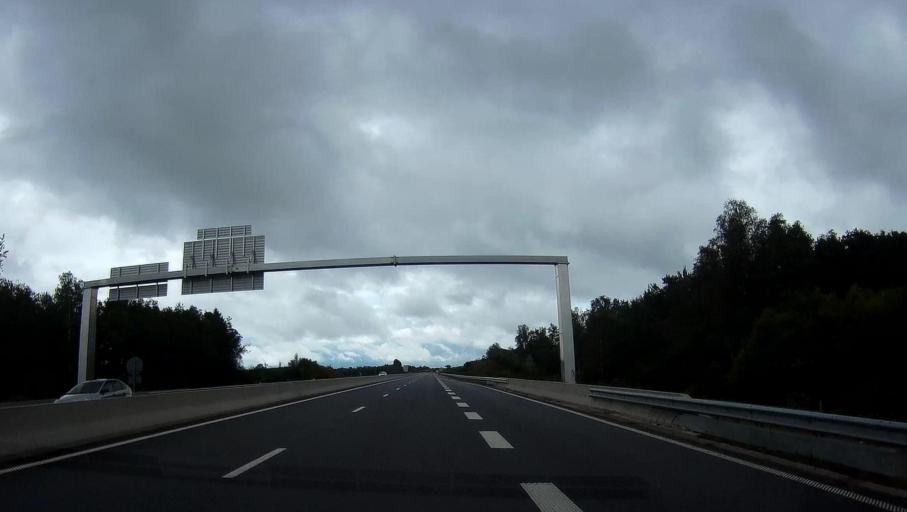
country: FR
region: Champagne-Ardenne
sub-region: Departement des Ardennes
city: Rocroi
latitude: 49.8986
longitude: 4.5212
